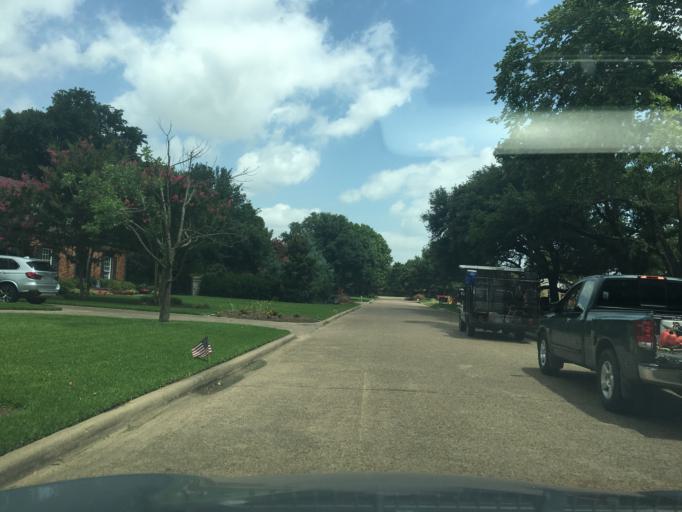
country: US
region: Texas
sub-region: Dallas County
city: Addison
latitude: 32.9123
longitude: -96.8247
